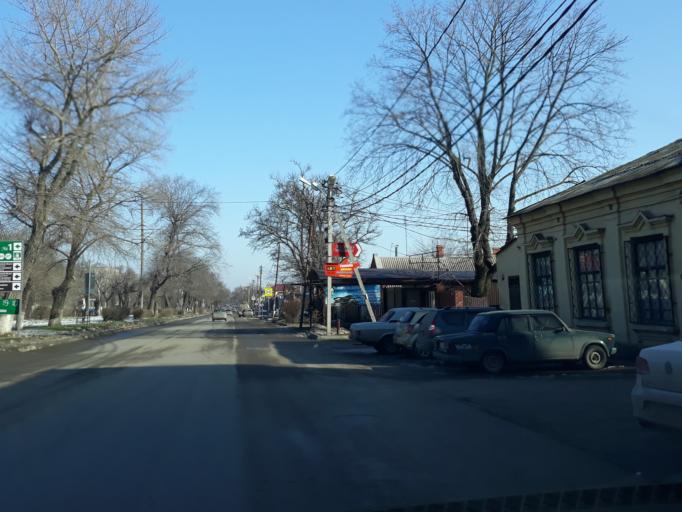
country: RU
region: Rostov
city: Taganrog
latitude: 47.2066
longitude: 38.9065
